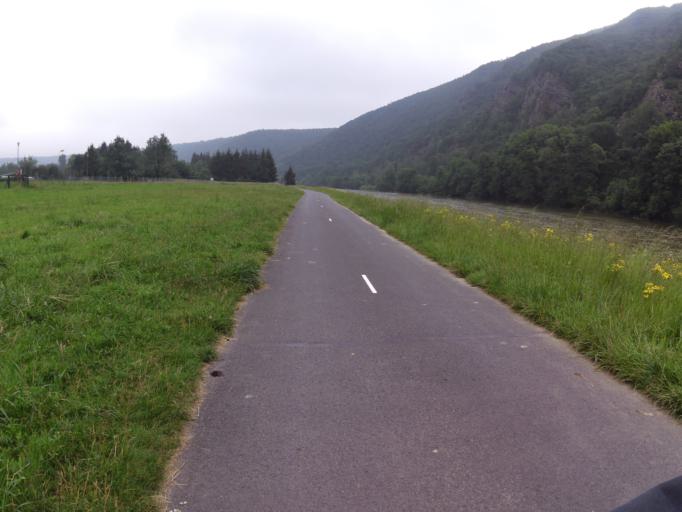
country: FR
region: Champagne-Ardenne
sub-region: Departement des Ardennes
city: Fumay
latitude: 49.9866
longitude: 4.7135
